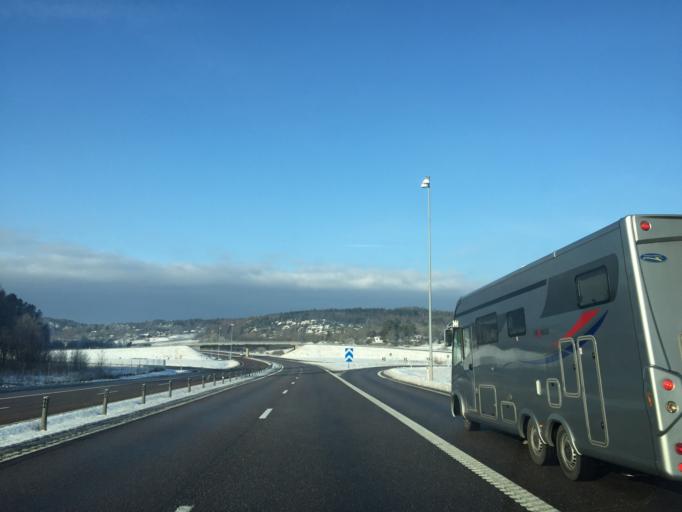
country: SE
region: Vaestra Goetaland
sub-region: Tanums Kommun
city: Tanumshede
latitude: 58.7326
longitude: 11.3297
